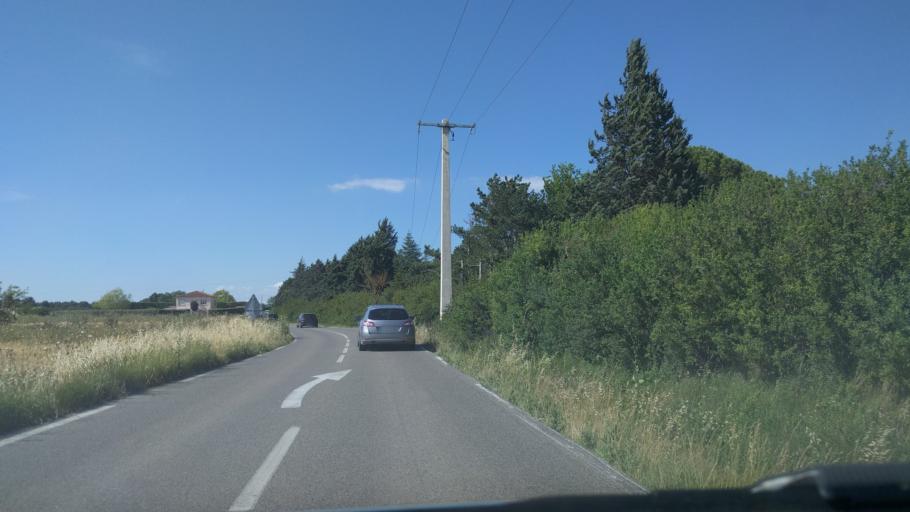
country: FR
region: Provence-Alpes-Cote d'Azur
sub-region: Departement des Bouches-du-Rhone
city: Eguilles
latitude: 43.5102
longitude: 5.3501
